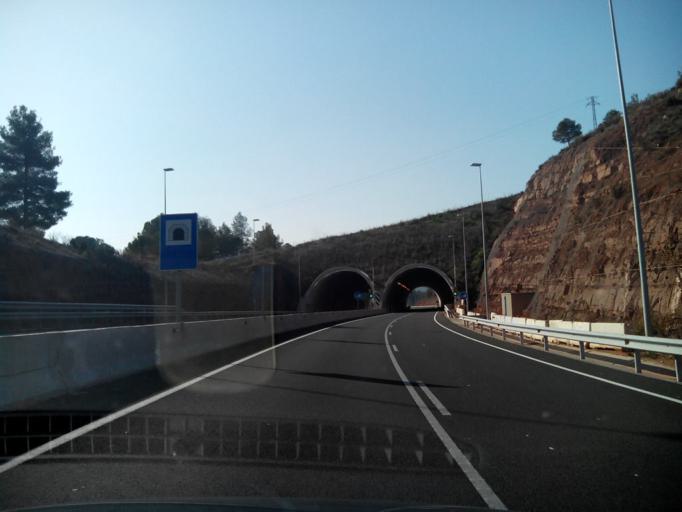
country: ES
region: Catalonia
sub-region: Provincia de Barcelona
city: Sant Joan de Vilatorrada
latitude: 41.7321
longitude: 1.7806
